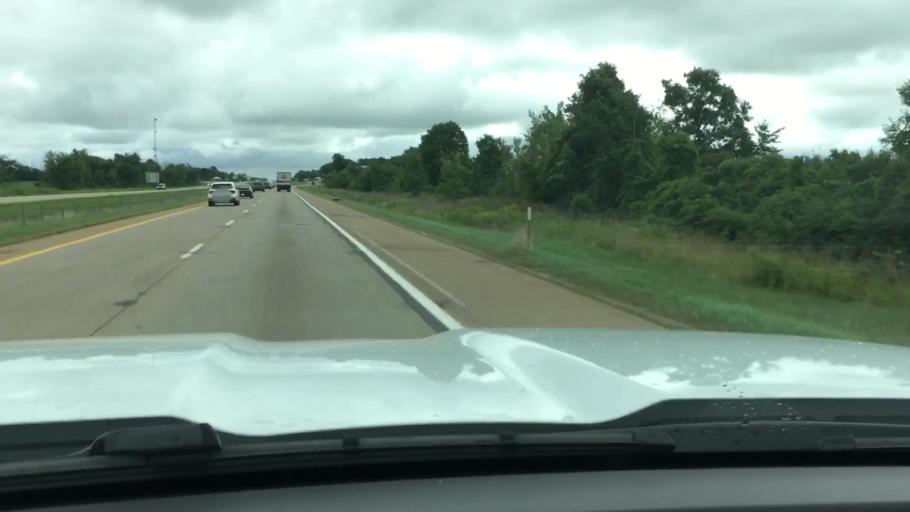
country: US
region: Michigan
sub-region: Ionia County
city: Ionia
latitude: 42.8787
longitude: -85.0495
